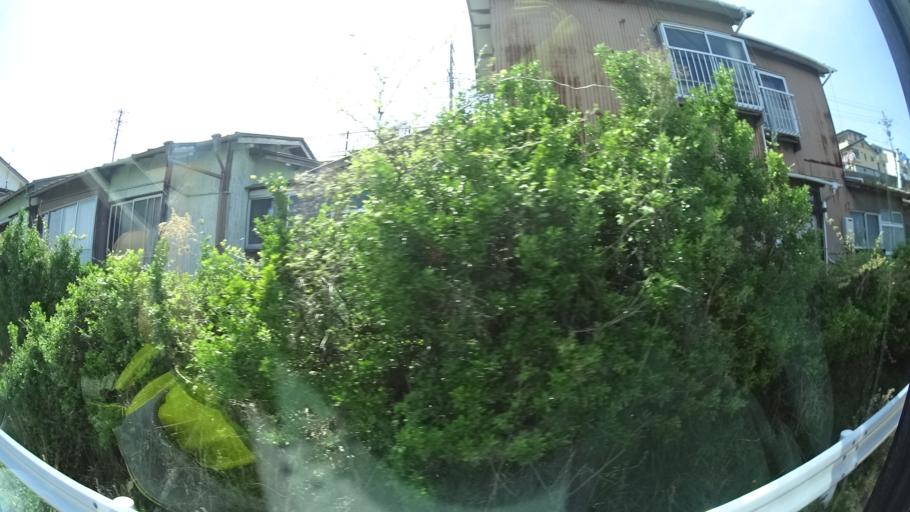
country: JP
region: Iwate
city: Ofunato
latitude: 39.0523
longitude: 141.7205
